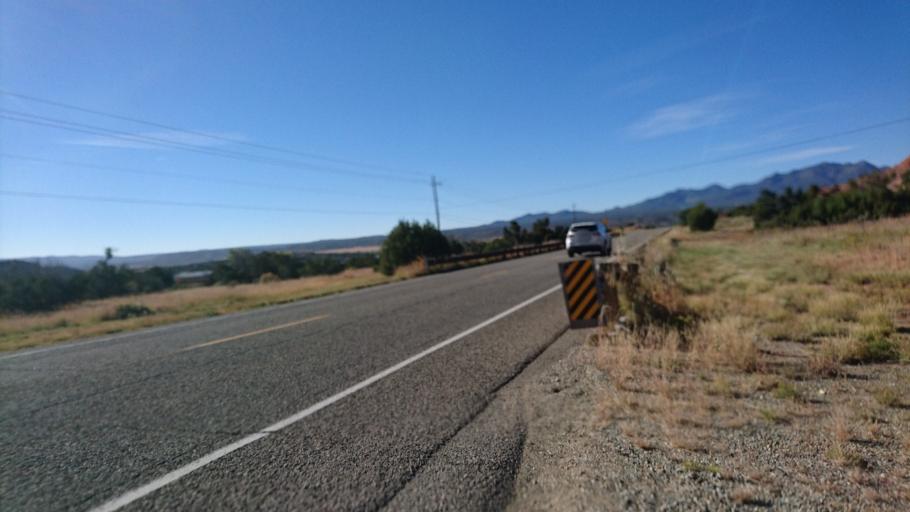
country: US
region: New Mexico
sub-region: Santa Fe County
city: La Cienega
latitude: 35.4413
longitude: -106.0802
